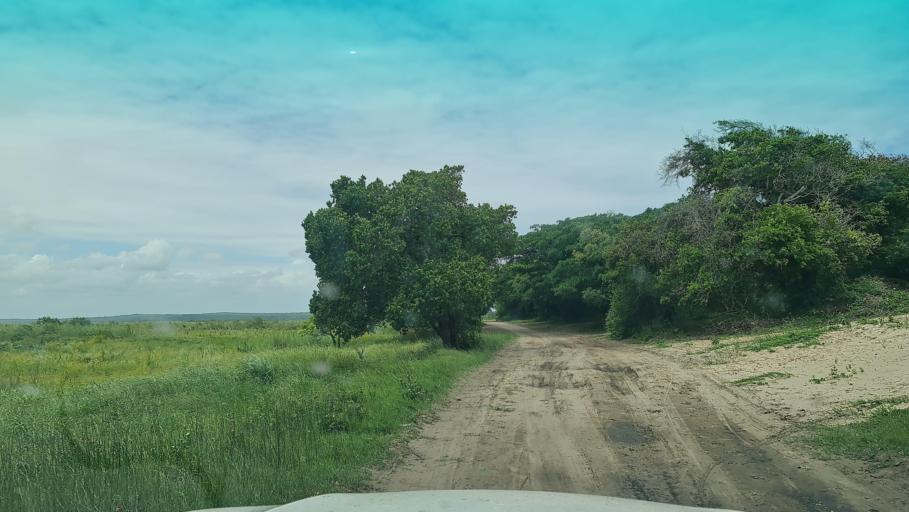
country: MZ
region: Maputo
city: Manhica
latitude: -25.5303
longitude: 32.8458
